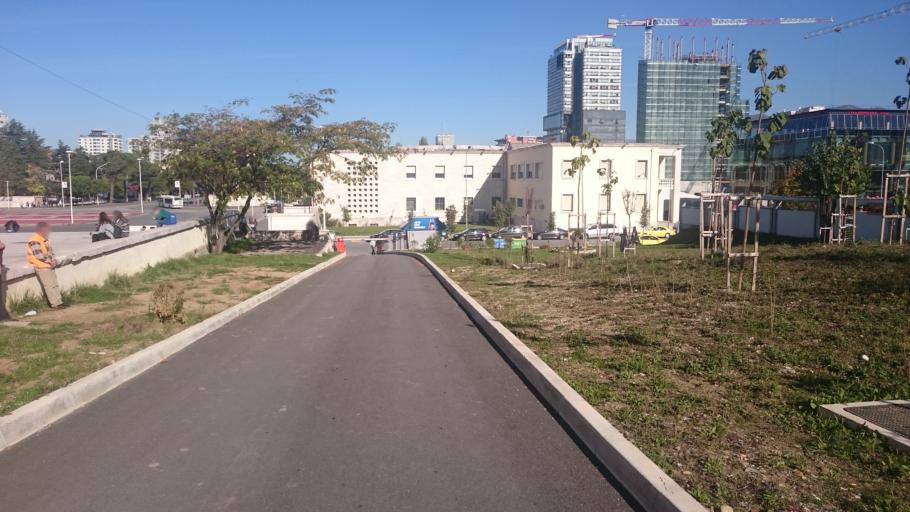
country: AL
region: Tirane
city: Tirana
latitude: 41.3169
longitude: 19.8223
